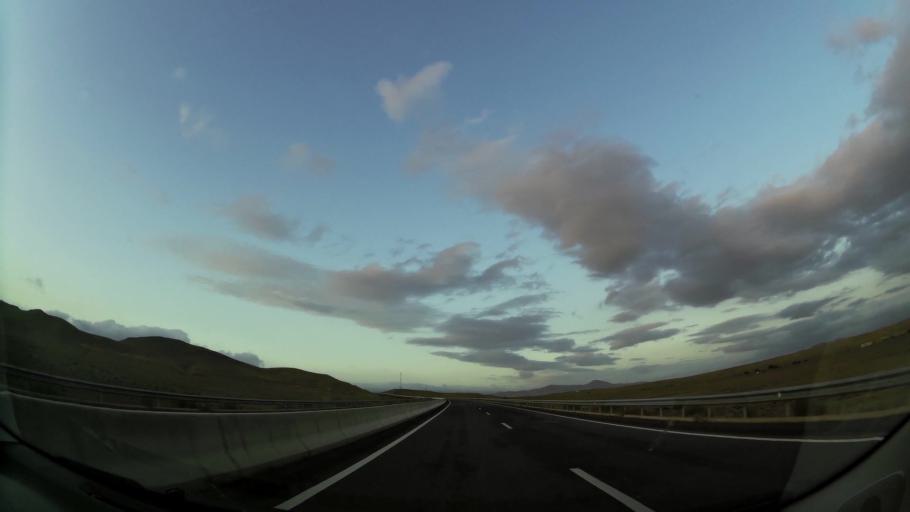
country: MA
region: Oriental
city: Taourirt
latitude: 34.5895
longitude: -2.7878
